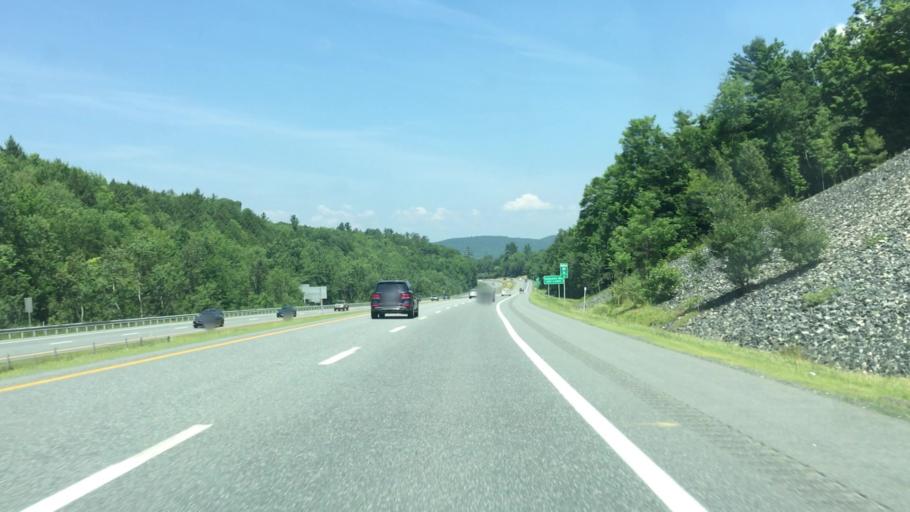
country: US
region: New Hampshire
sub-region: Grafton County
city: Enfield
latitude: 43.6172
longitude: -72.1954
